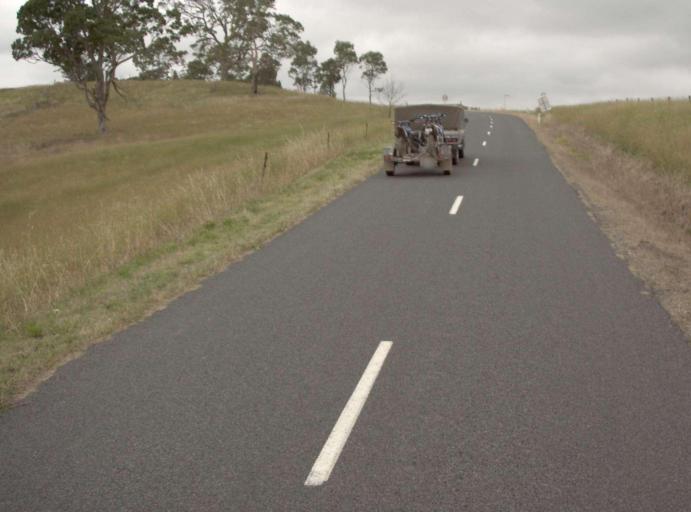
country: AU
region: Victoria
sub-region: Wellington
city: Heyfield
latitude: -37.8693
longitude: 146.7066
